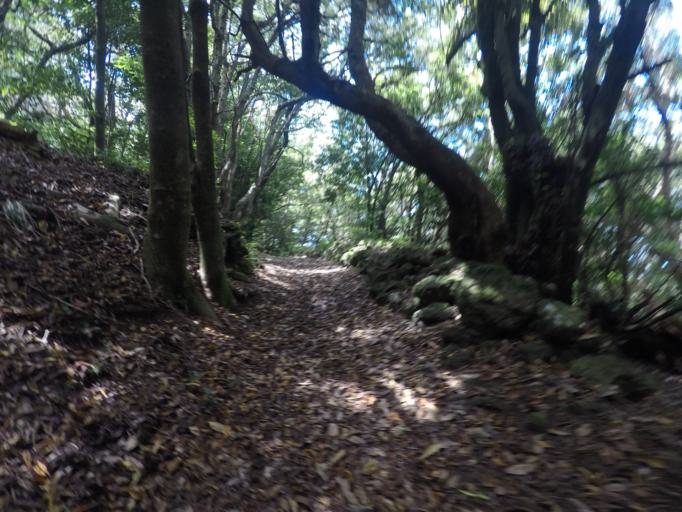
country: PT
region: Madeira
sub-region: Porto Moniz
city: Porto Moniz
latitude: 32.8372
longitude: -17.1439
